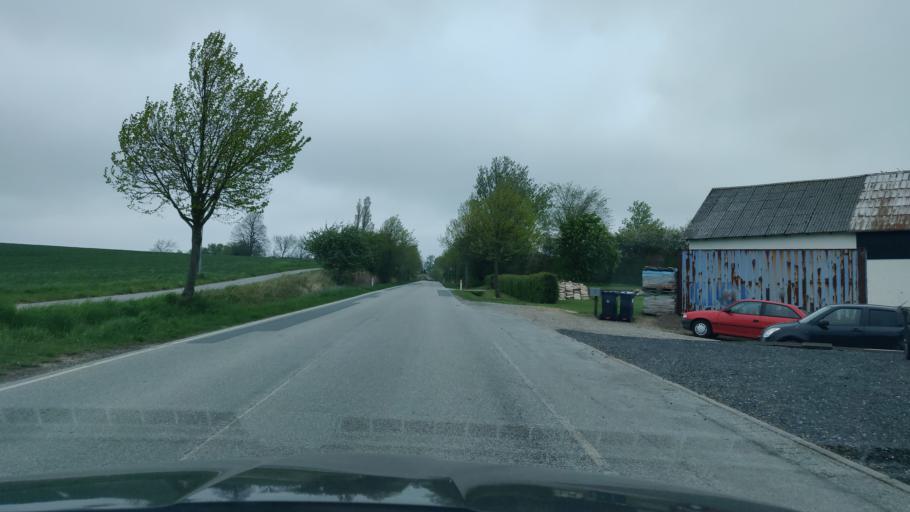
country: DK
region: South Denmark
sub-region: Sonderborg Kommune
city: Guderup
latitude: 54.9899
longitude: 9.8881
